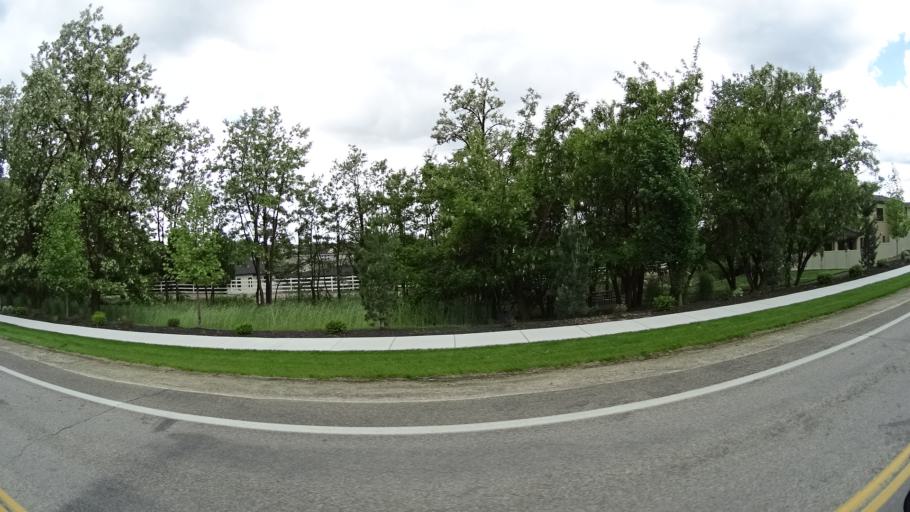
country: US
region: Idaho
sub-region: Ada County
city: Garden City
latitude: 43.6761
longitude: -116.2637
